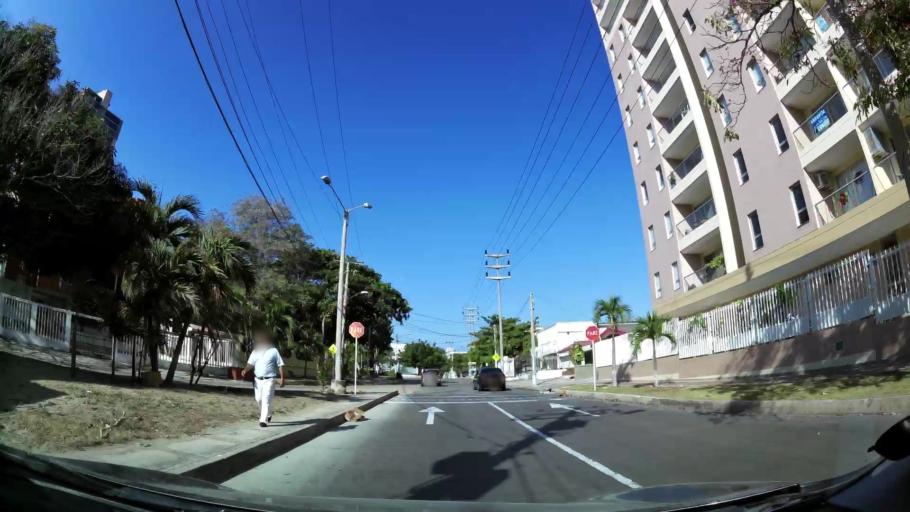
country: CO
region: Atlantico
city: Barranquilla
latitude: 11.0118
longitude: -74.8095
